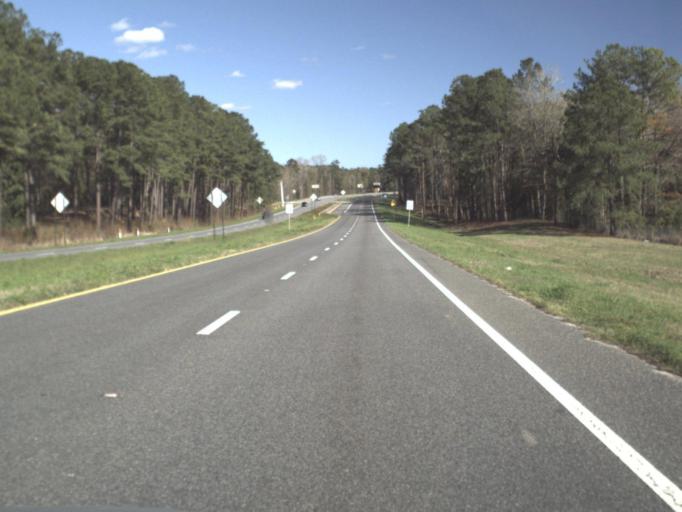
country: US
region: Florida
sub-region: Gadsden County
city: Midway
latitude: 30.5523
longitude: -84.4983
